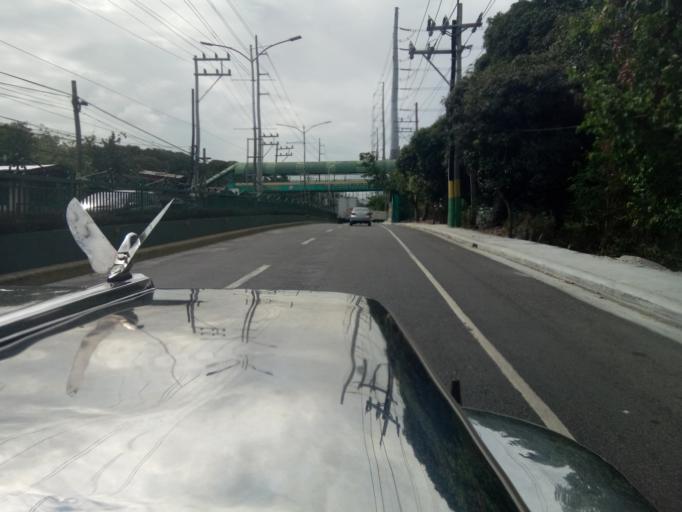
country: PH
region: Calabarzon
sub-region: Province of Cavite
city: Dasmarinas
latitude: 14.3121
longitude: 120.9482
